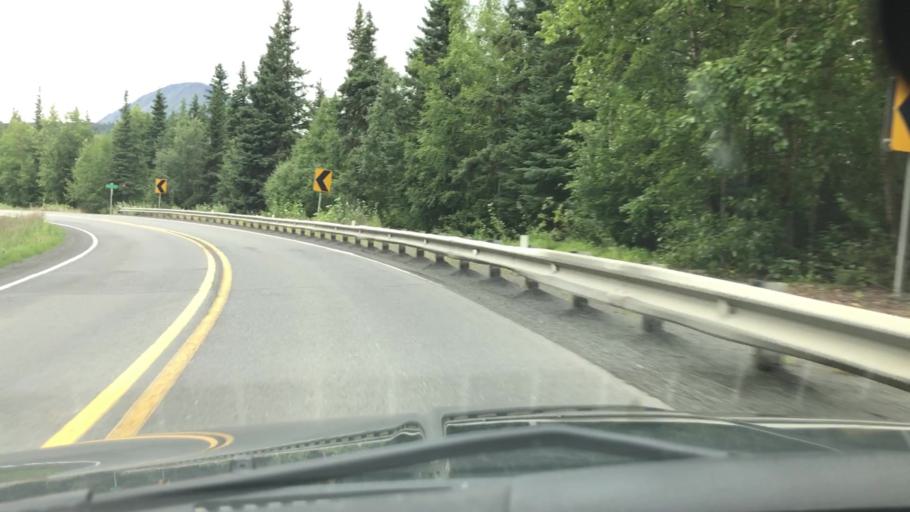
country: US
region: Alaska
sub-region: Kenai Peninsula Borough
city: Seward
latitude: 60.4864
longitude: -149.8574
